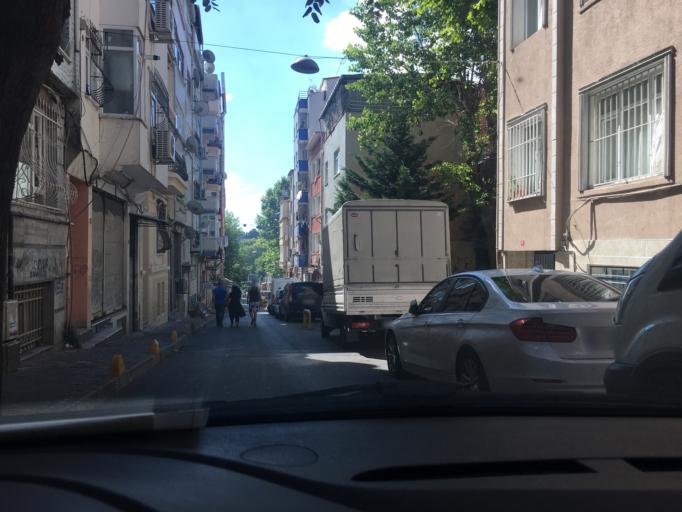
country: TR
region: Istanbul
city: Istanbul
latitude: 41.0176
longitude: 28.9538
